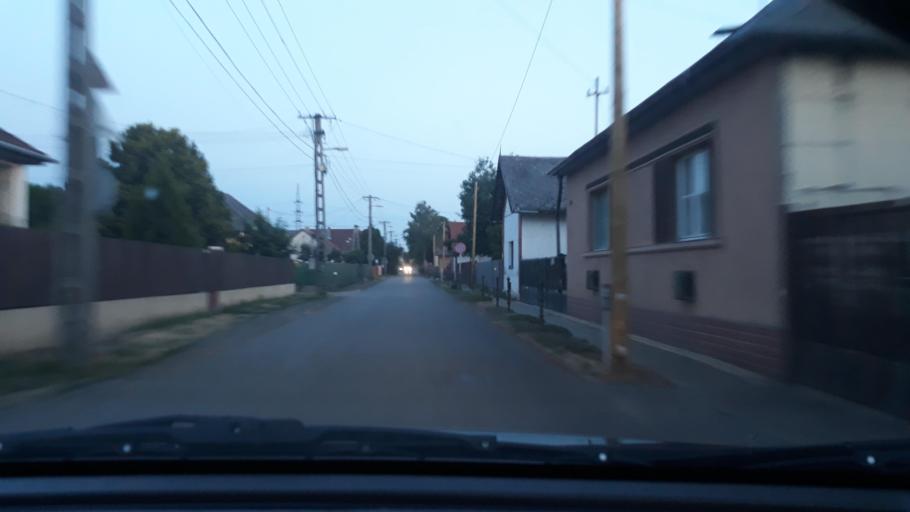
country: HU
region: Hajdu-Bihar
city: Debrecen
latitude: 47.5332
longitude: 21.6660
